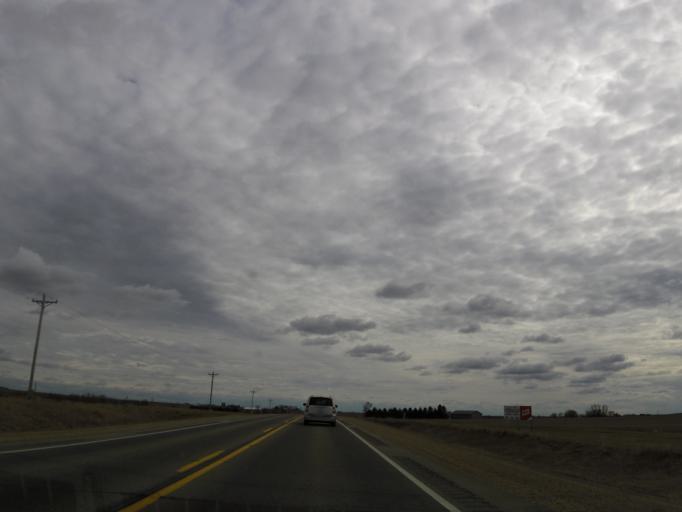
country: US
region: Iowa
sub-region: Chickasaw County
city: New Hampton
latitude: 43.1486
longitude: -92.2990
